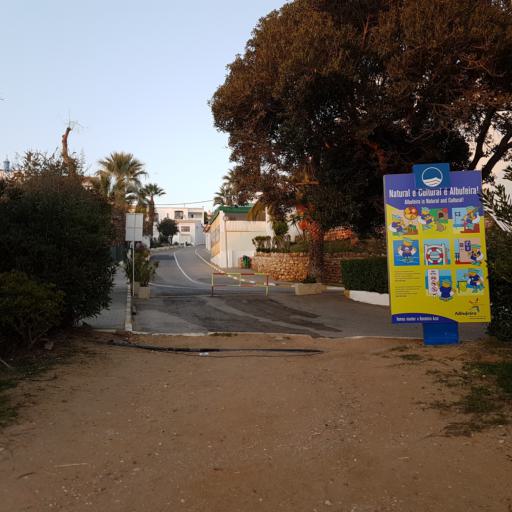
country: PT
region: Faro
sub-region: Albufeira
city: Albufeira
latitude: 37.0846
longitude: -8.2371
